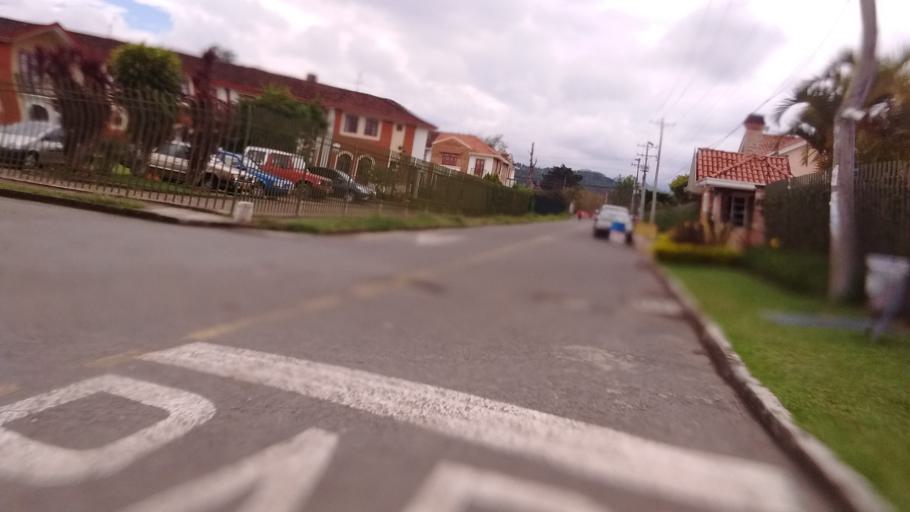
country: CO
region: Cauca
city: Popayan
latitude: 2.4775
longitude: -76.5807
